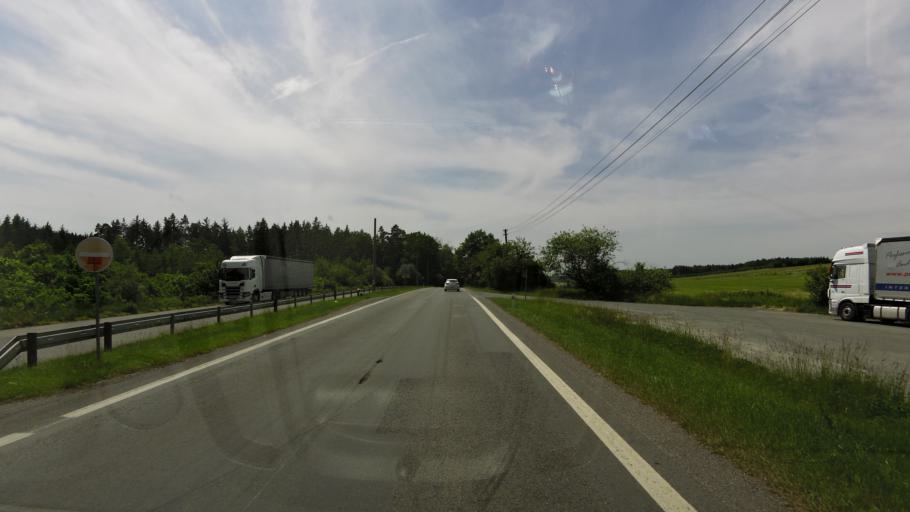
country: CZ
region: Plzensky
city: Zbiroh
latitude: 49.8295
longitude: 13.7962
